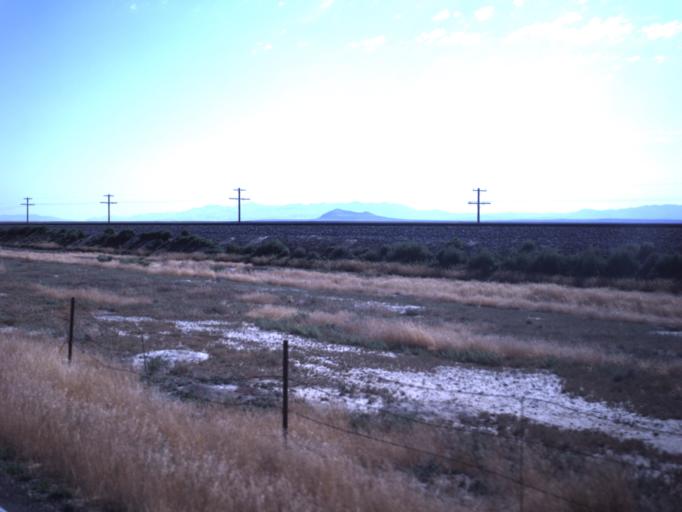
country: US
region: Utah
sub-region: Millard County
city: Delta
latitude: 38.9989
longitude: -112.7879
